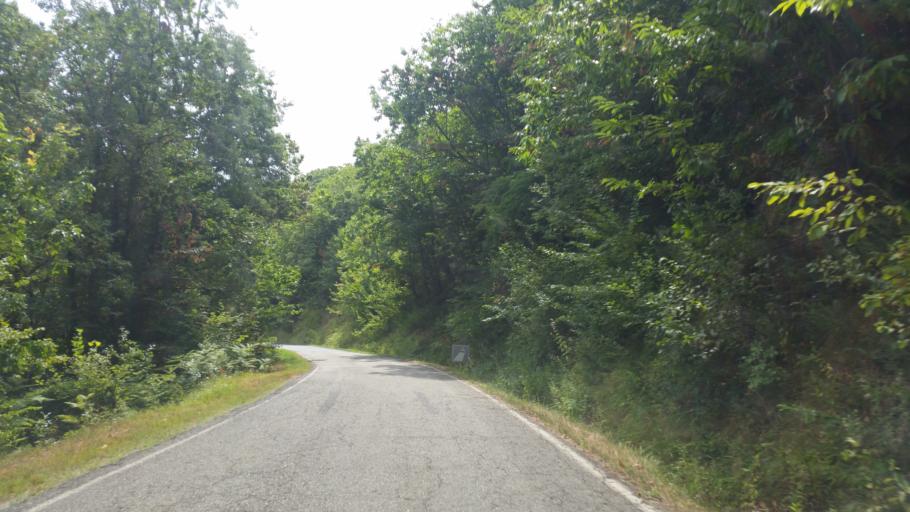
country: IT
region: Piedmont
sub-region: Provincia di Asti
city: Vesime
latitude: 44.6482
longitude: 8.2243
